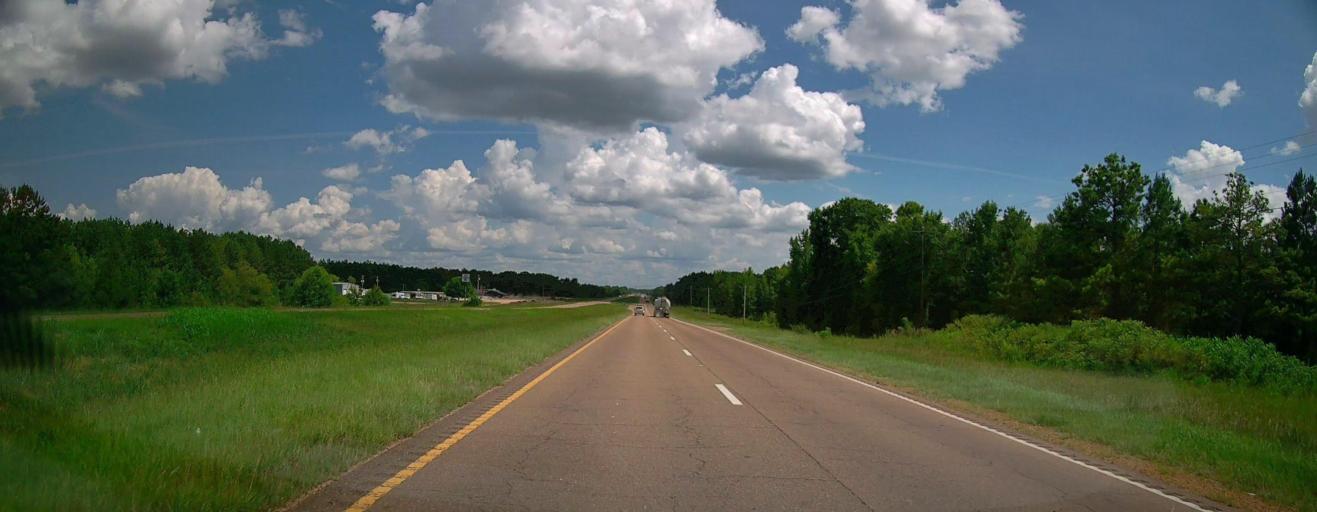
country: US
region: Mississippi
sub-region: Lowndes County
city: Columbus Air Force Base
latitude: 33.6881
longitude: -88.4374
